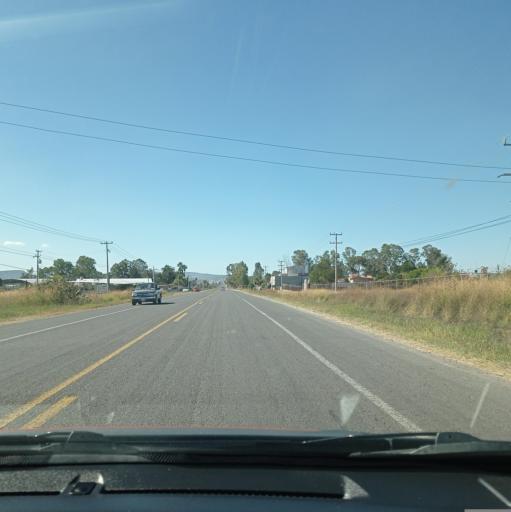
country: MX
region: Jalisco
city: San Miguel el Alto
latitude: 21.0199
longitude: -102.3467
